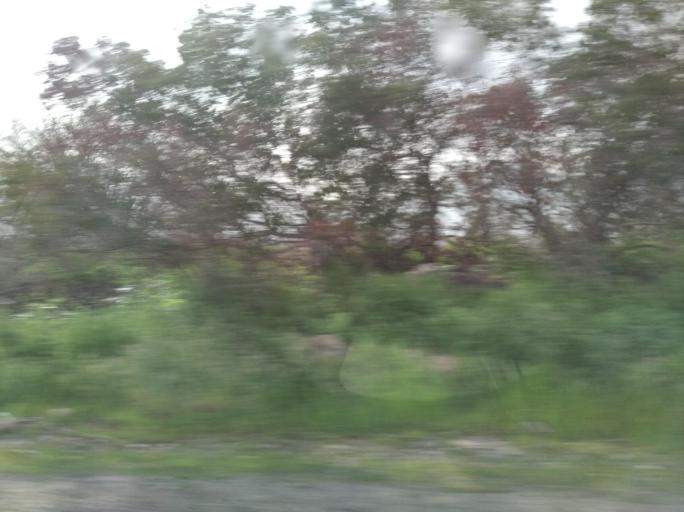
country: CL
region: Santiago Metropolitan
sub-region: Provincia de Chacabuco
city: Lampa
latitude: -33.1318
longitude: -70.9206
